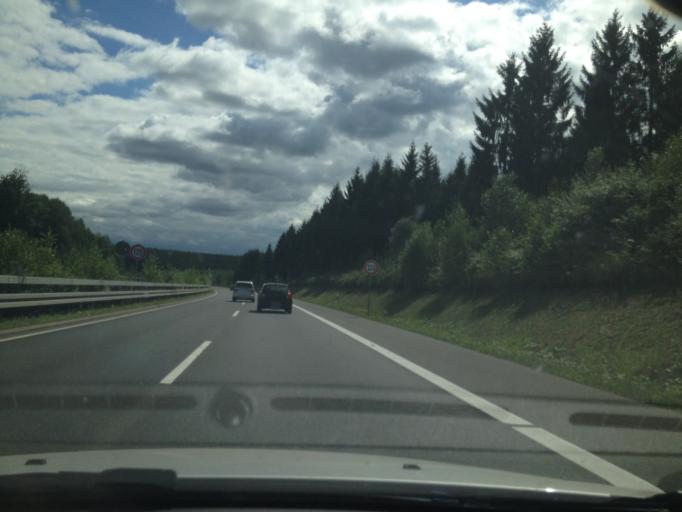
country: DE
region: North Rhine-Westphalia
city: Kreuztal
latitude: 50.9776
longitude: 7.9398
